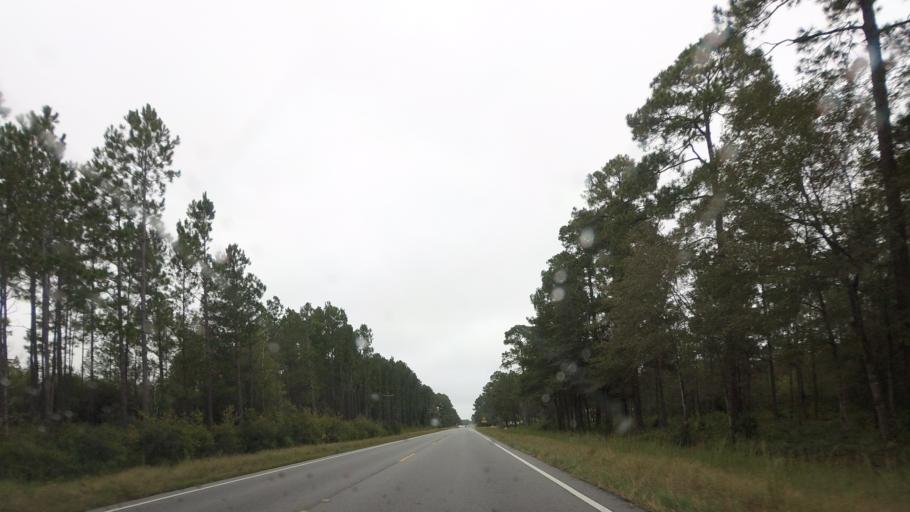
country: US
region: Georgia
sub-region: Berrien County
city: Nashville
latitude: 31.2689
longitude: -83.2396
